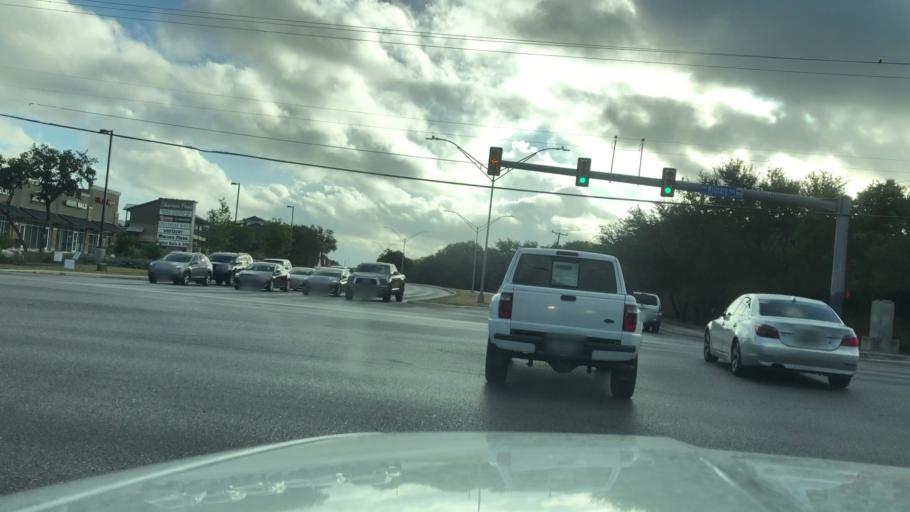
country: US
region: Texas
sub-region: Bexar County
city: Shavano Park
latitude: 29.5749
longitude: -98.5448
